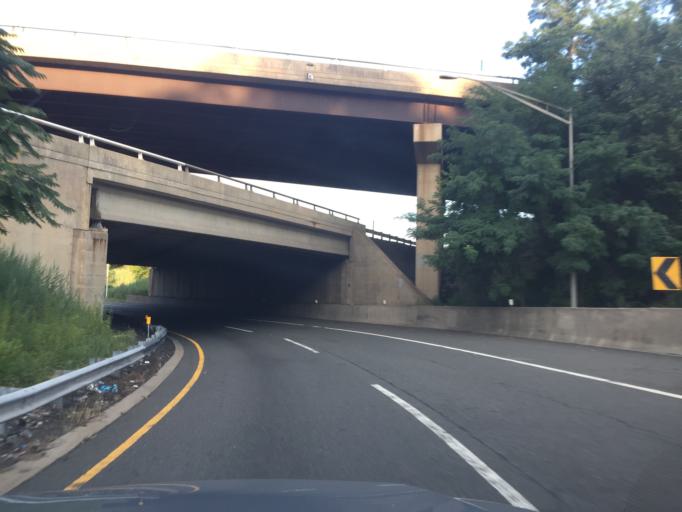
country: US
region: New Jersey
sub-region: Middlesex County
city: Fords
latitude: 40.5387
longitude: -74.3071
